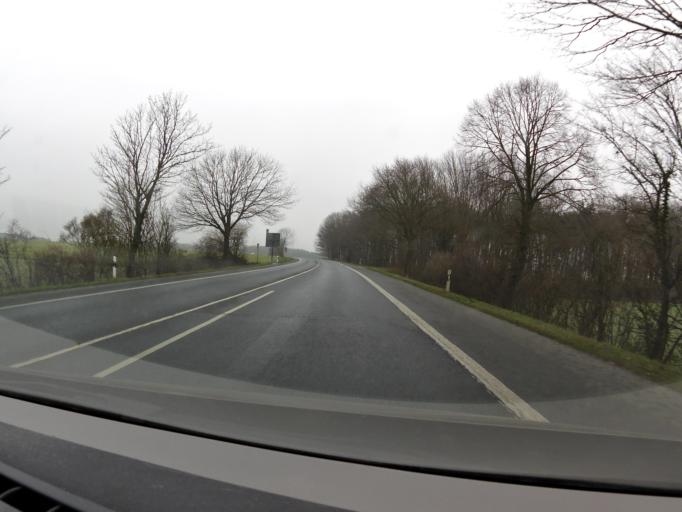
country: DE
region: North Rhine-Westphalia
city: Straelen
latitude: 51.3904
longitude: 6.2674
